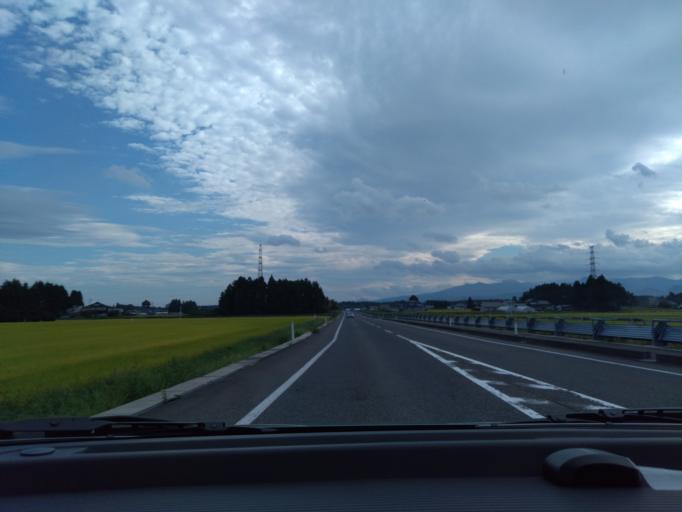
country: JP
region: Iwate
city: Hanamaki
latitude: 39.3434
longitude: 141.0513
